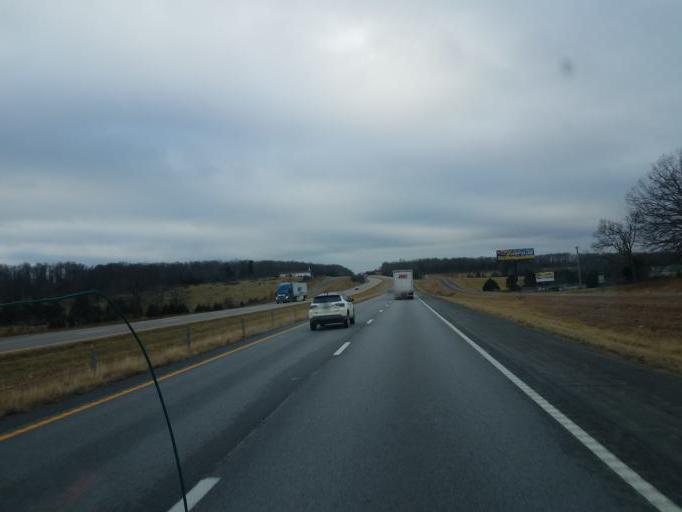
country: US
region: Missouri
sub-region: Webster County
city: Marshfield
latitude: 37.5290
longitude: -92.8273
